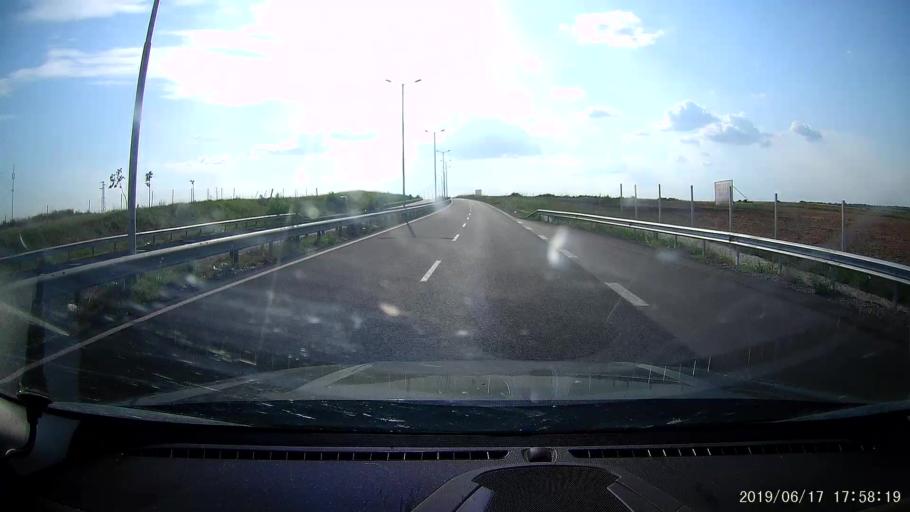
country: BG
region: Khaskovo
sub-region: Obshtina Svilengrad
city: Svilengrad
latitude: 41.7255
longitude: 26.3231
